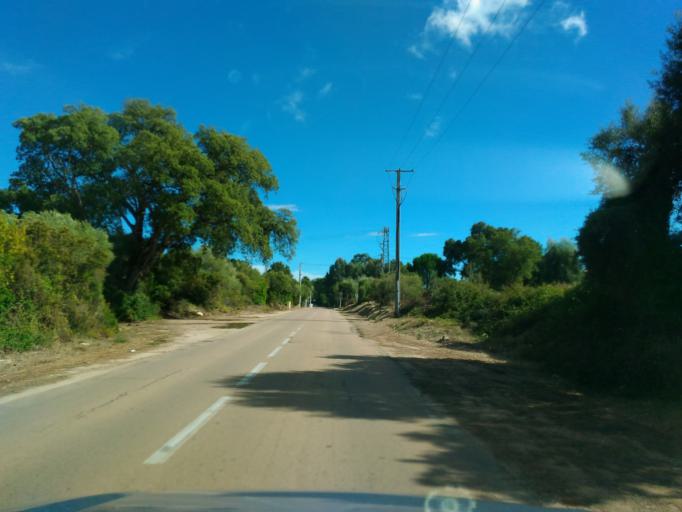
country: FR
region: Corsica
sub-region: Departement de la Corse-du-Sud
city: Porto-Vecchio
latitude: 41.7017
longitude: 9.3388
